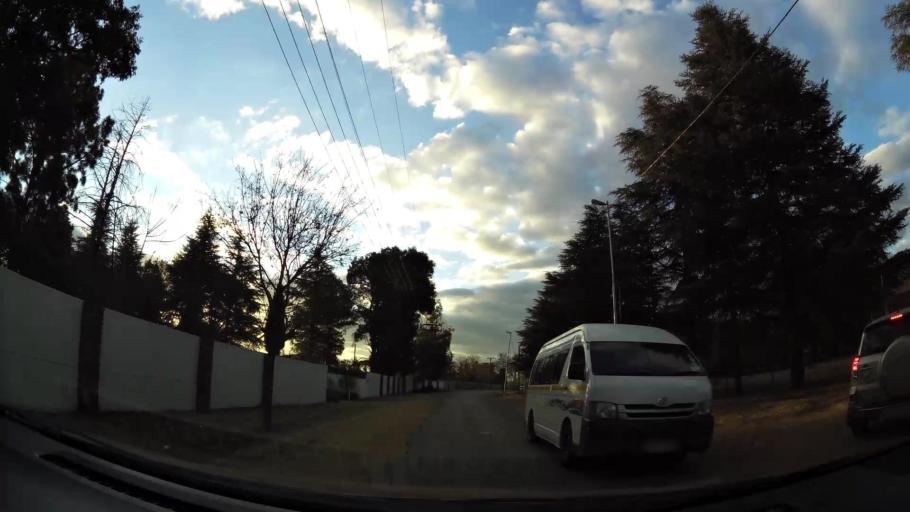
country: ZA
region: Gauteng
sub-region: City of Johannesburg Metropolitan Municipality
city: Midrand
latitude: -26.0071
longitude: 28.1533
